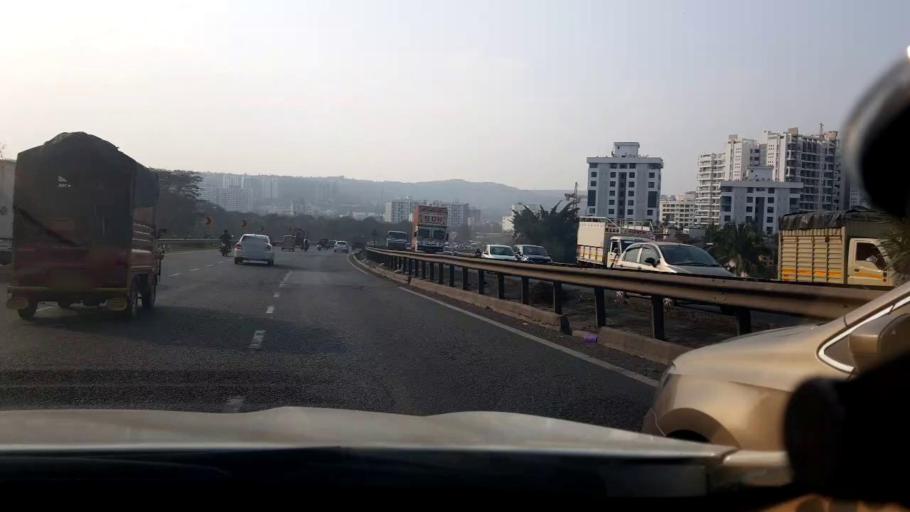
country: IN
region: Maharashtra
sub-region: Pune Division
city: Kharakvasla
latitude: 18.5089
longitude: 73.7760
